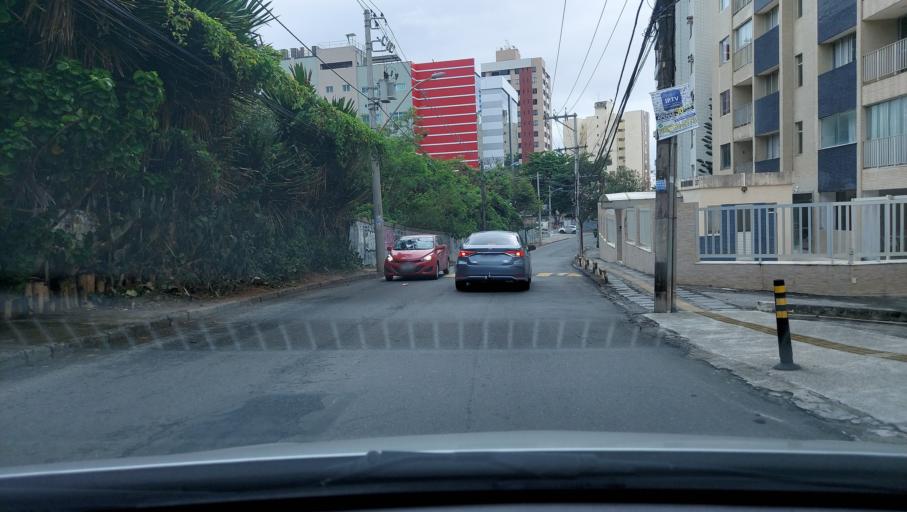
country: BR
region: Bahia
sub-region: Salvador
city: Salvador
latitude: -12.9880
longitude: -38.4447
